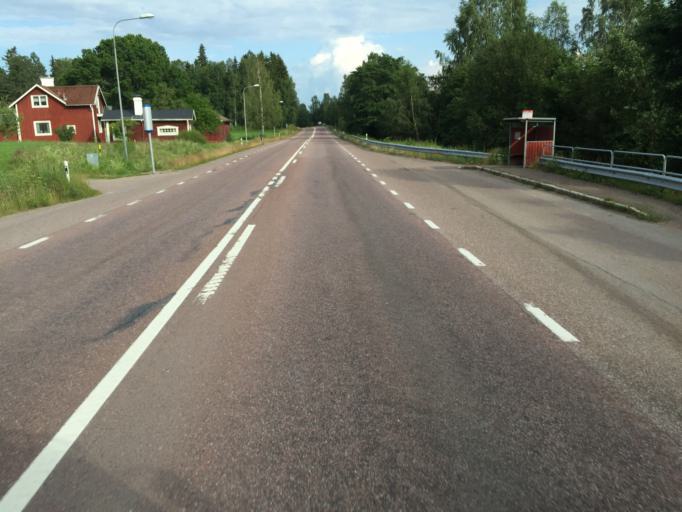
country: SE
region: Dalarna
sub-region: Borlange Kommun
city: Borlaenge
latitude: 60.5341
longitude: 15.2995
